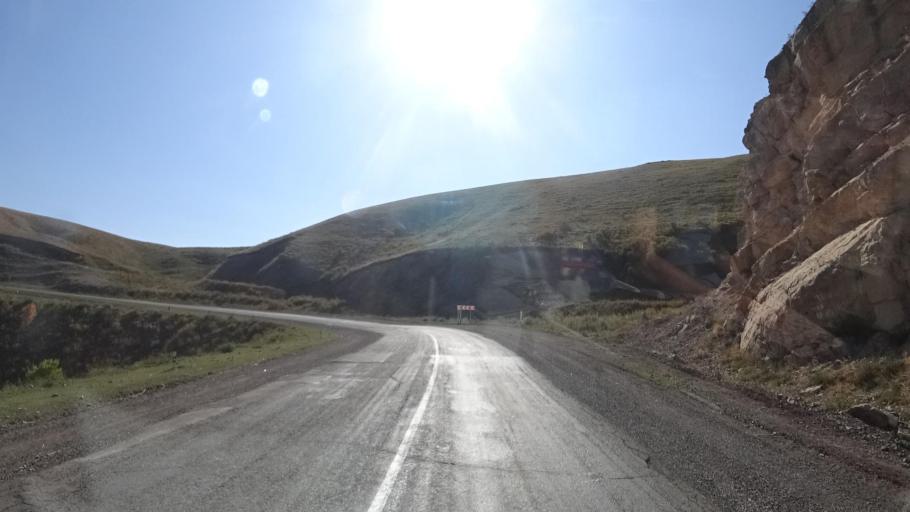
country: KZ
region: Almaty Oblysy
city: Kegen
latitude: 43.1450
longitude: 79.1977
